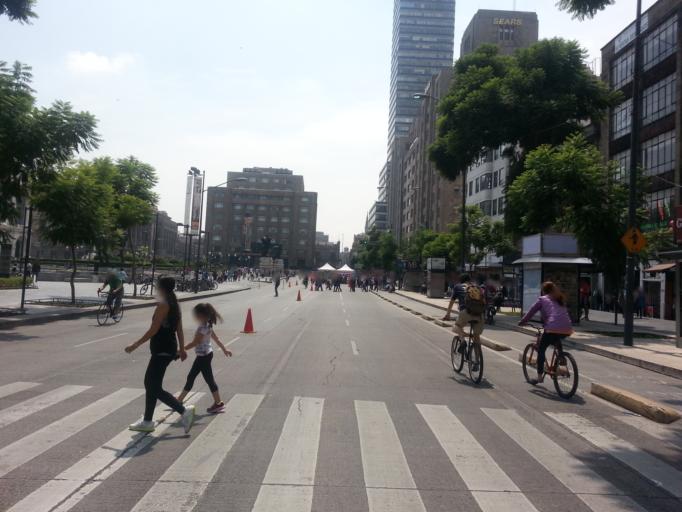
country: MX
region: Mexico City
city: Cuauhtemoc
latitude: 19.4345
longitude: -99.1427
